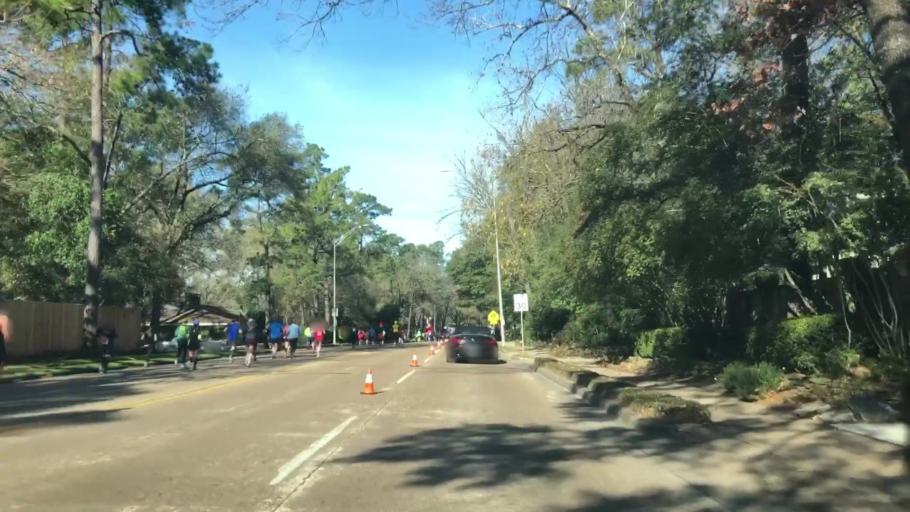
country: US
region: Texas
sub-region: Harris County
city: Hunters Creek Village
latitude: 29.7751
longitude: -95.4816
